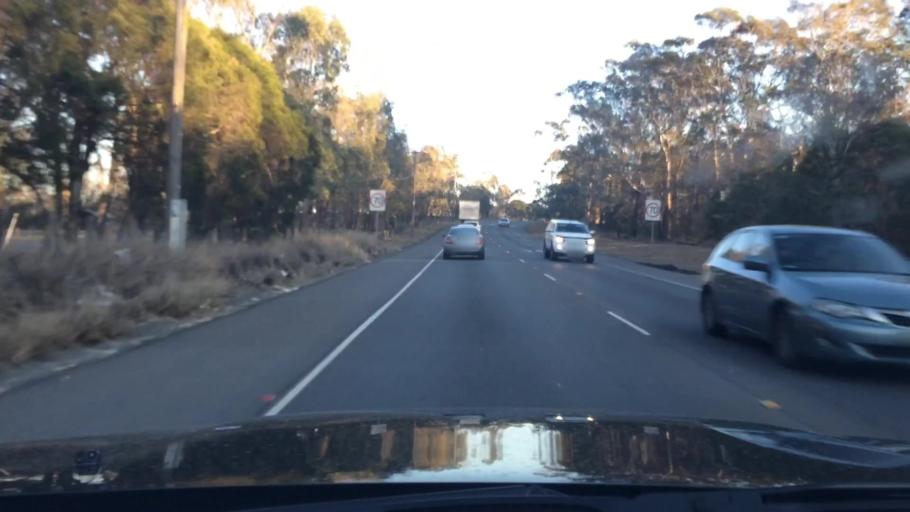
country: AU
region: New South Wales
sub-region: Fairfield
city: Carramar
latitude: -33.9021
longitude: 150.9780
